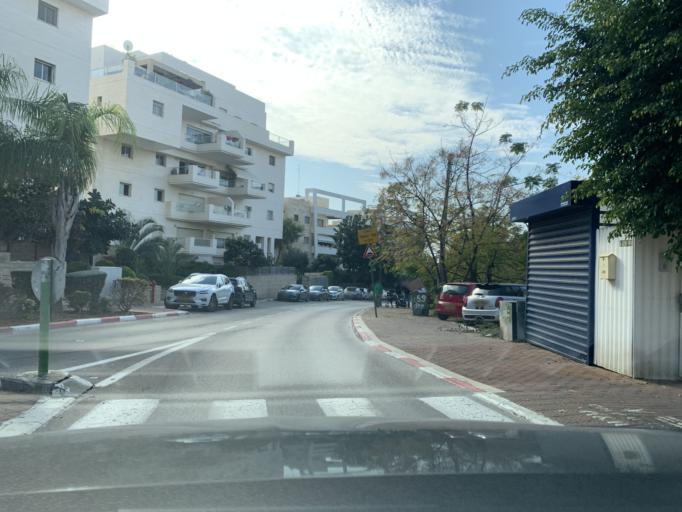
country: IL
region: Tel Aviv
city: Giv`at Shemu'el
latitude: 32.0626
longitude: 34.8490
